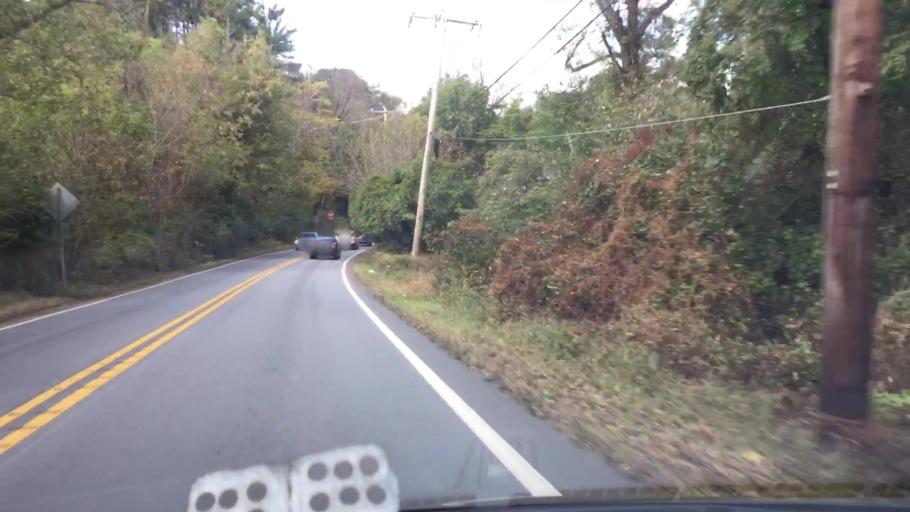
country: US
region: Pennsylvania
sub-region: Delaware County
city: Lima
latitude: 39.9589
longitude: -75.4320
